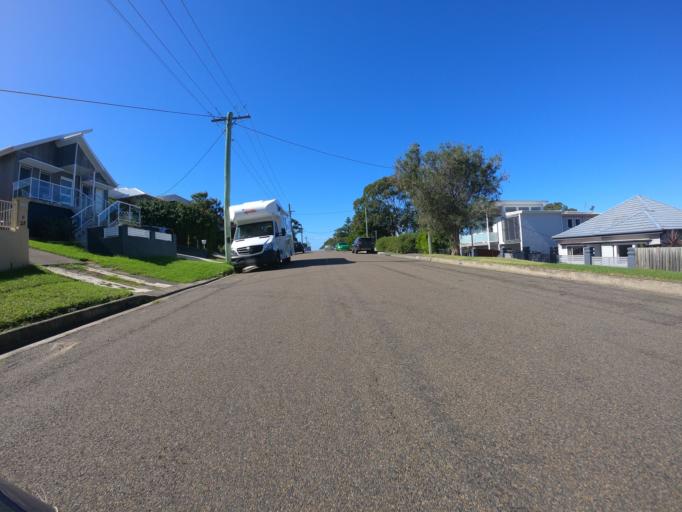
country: AU
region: New South Wales
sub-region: Wollongong
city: Bulli
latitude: -34.3403
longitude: 150.9174
